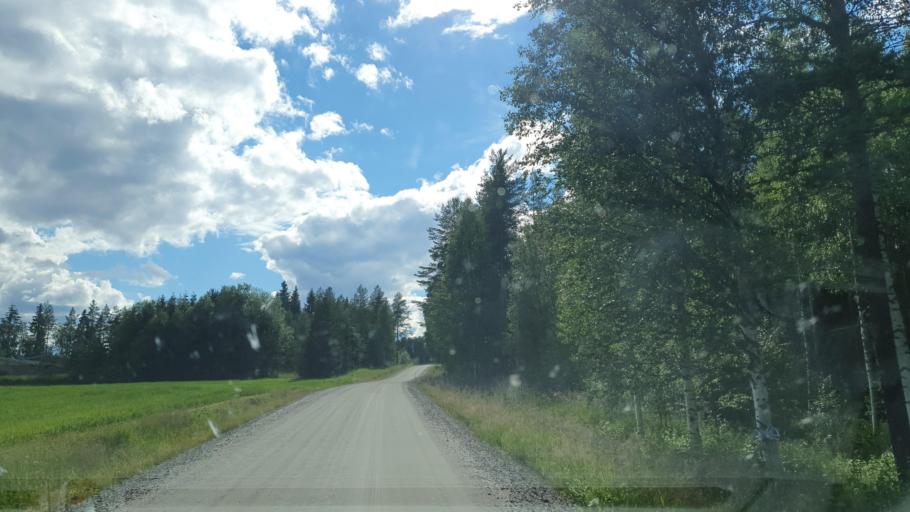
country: FI
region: Kainuu
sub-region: Kehys-Kainuu
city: Kuhmo
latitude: 64.1306
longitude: 29.6521
